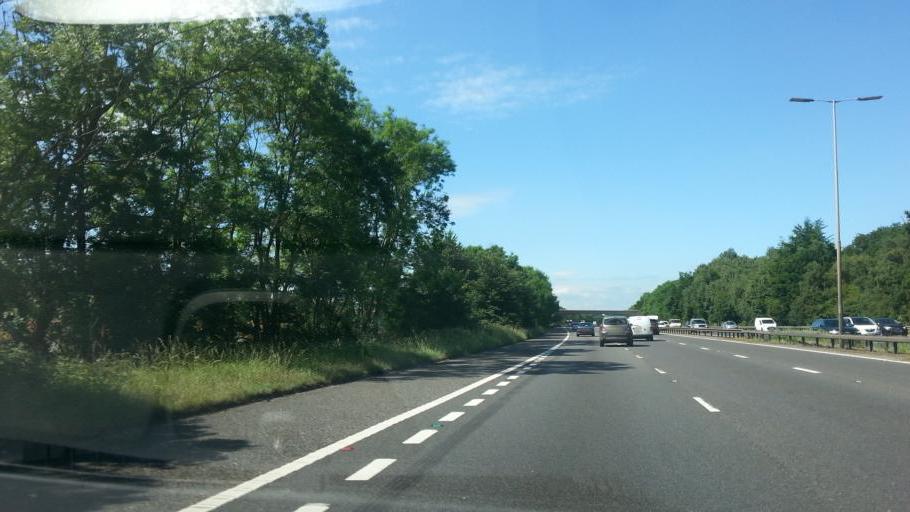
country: GB
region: England
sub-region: Royal Borough of Windsor and Maidenhead
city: Maidenhead
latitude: 51.4961
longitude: -0.7324
